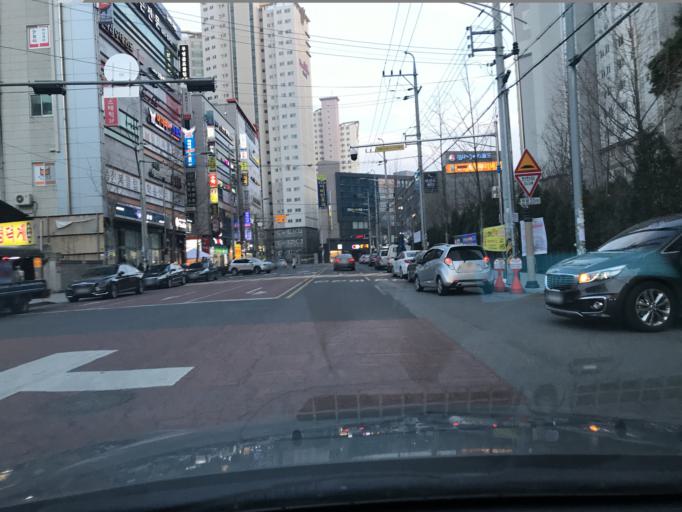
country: KR
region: Daegu
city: Hwawon
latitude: 35.8157
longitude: 128.5196
